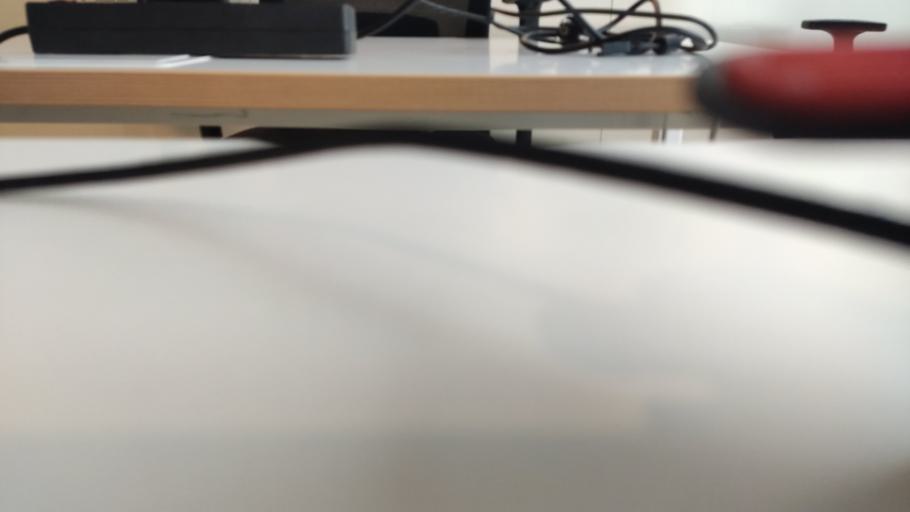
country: RU
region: Moskovskaya
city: Rogachevo
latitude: 56.4157
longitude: 37.0324
